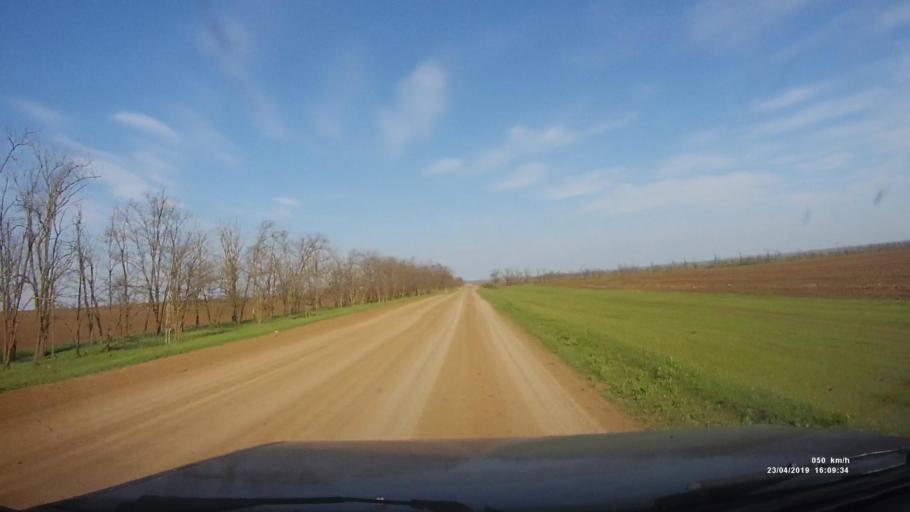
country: RU
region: Rostov
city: Remontnoye
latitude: 46.4816
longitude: 43.1123
